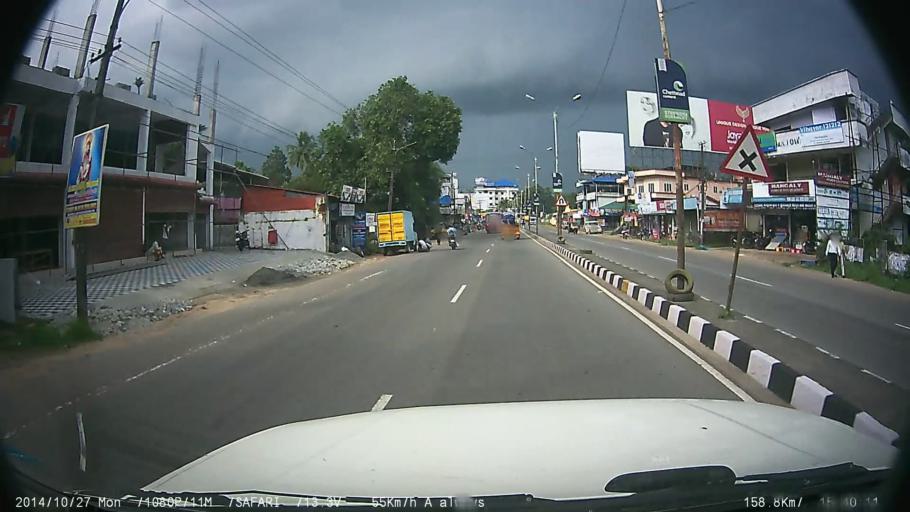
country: IN
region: Kerala
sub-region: Ernakulam
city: Angamali
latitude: 10.1855
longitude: 76.3807
